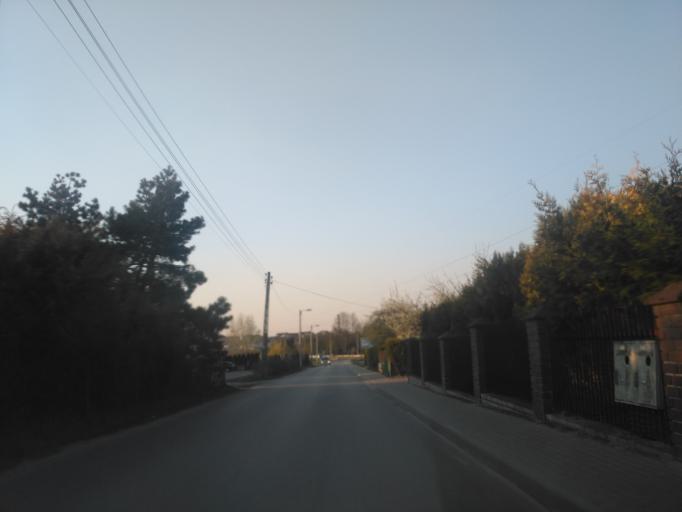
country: PL
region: Lublin Voivodeship
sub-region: Chelm
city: Chelm
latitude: 51.1204
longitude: 23.4839
